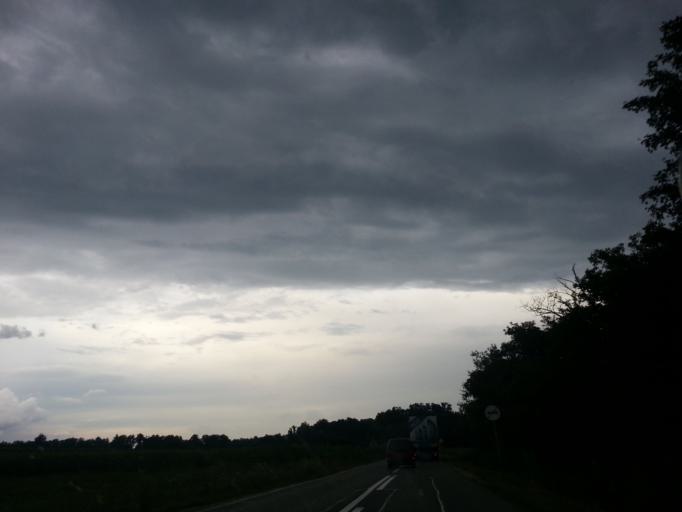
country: BA
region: Republika Srpska
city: Velika Obarska
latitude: 44.7923
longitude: 19.0850
